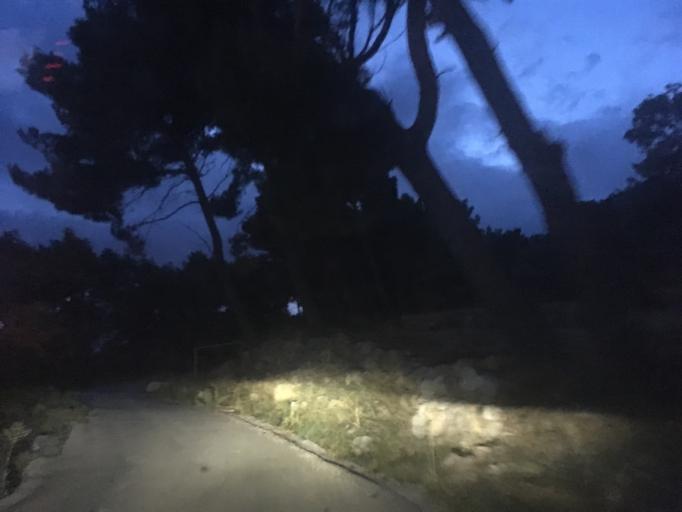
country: HR
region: Splitsko-Dalmatinska
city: Jesenice
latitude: 43.4629
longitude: 16.5965
